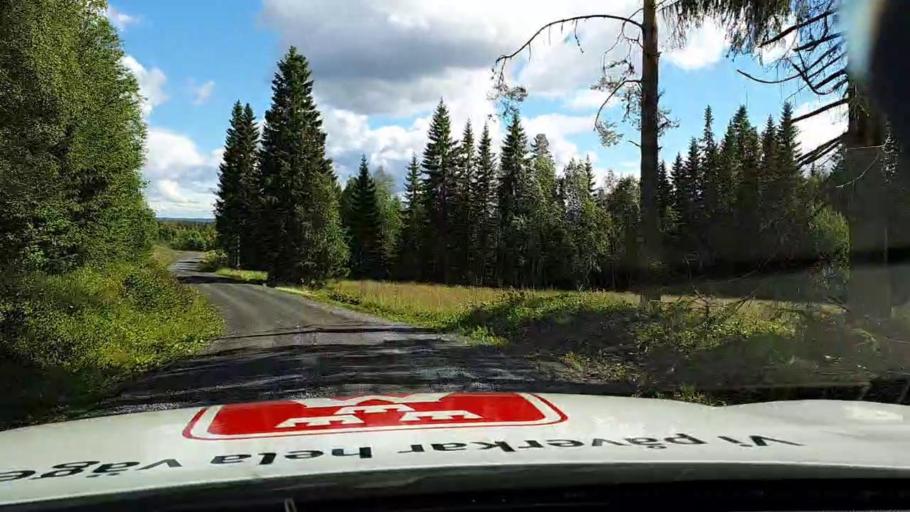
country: SE
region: Jaemtland
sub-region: Krokoms Kommun
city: Valla
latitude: 63.3279
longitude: 13.7351
